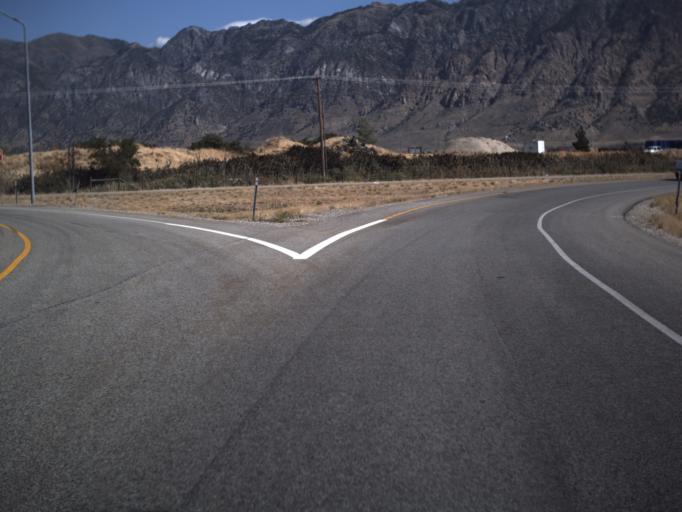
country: US
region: Utah
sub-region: Box Elder County
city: Brigham City
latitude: 41.5090
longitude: -112.0574
